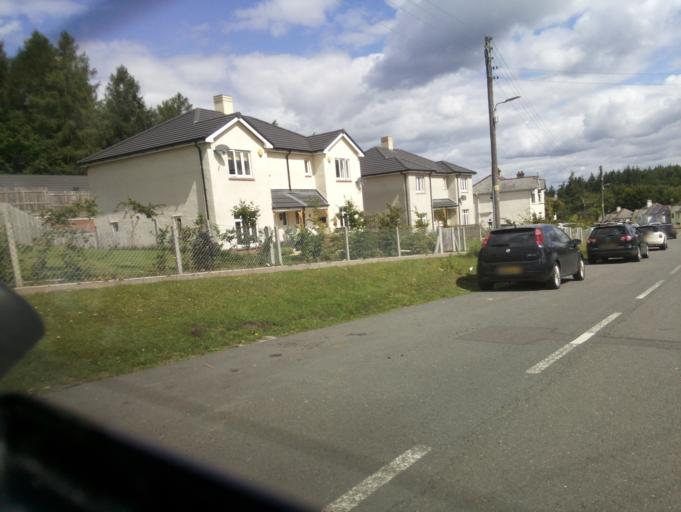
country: GB
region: England
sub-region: Gloucestershire
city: Bream
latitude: 51.7570
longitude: -2.5702
